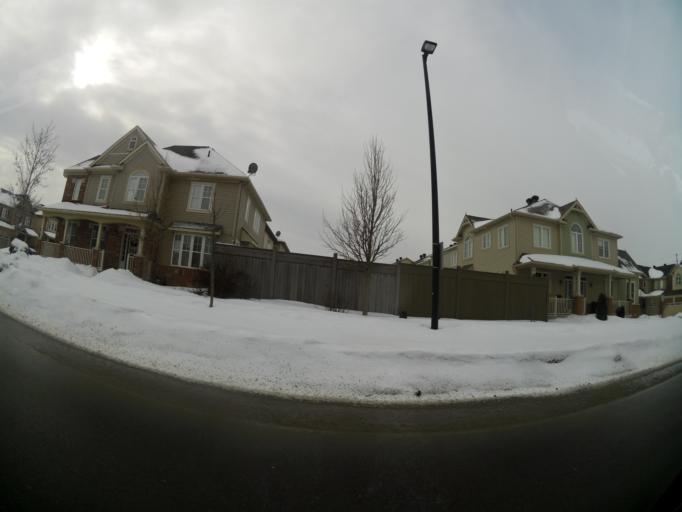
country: CA
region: Ontario
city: Bells Corners
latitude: 45.2882
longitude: -75.9195
